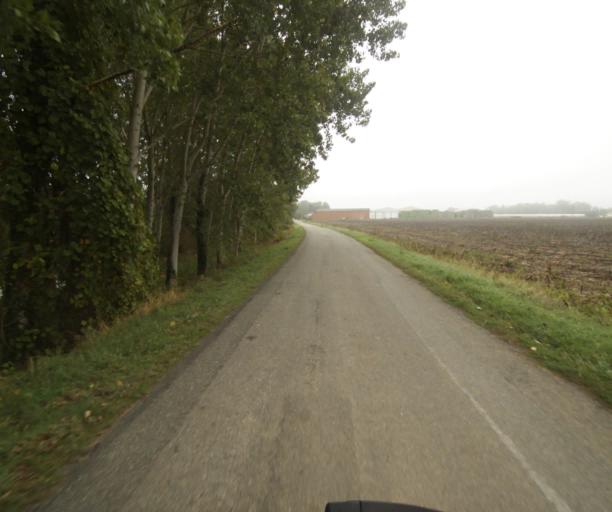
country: FR
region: Midi-Pyrenees
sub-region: Departement du Tarn-et-Garonne
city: Nohic
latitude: 43.9074
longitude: 1.4363
